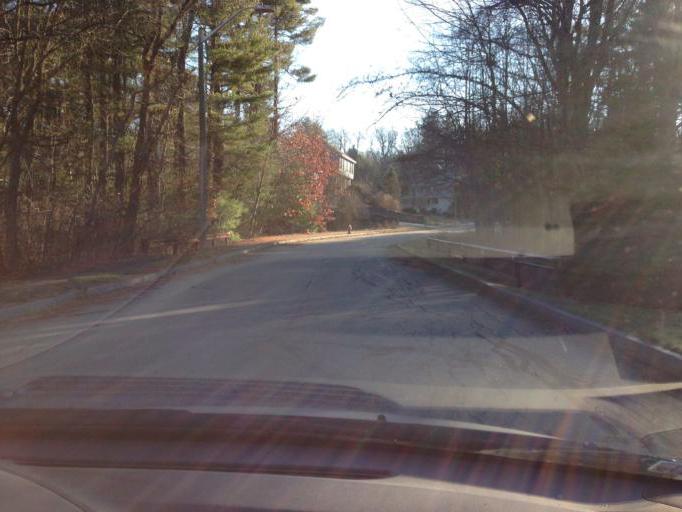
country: US
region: Massachusetts
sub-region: Middlesex County
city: Bedford
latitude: 42.5214
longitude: -71.2869
